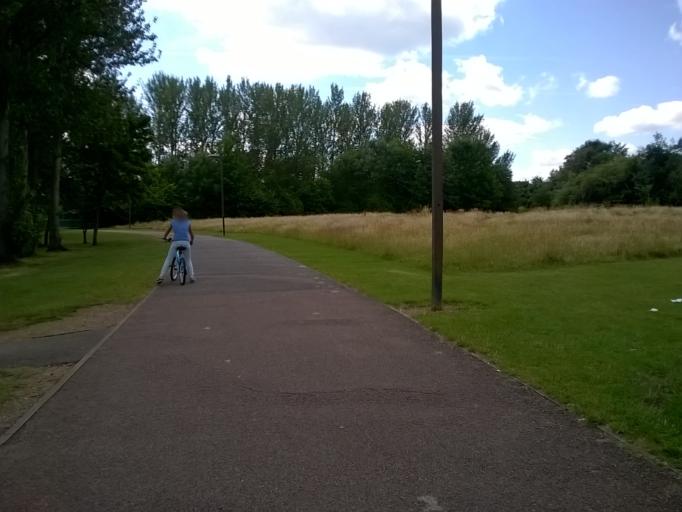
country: GB
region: England
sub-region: Milton Keynes
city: Broughton
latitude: 52.0533
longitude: -0.7251
